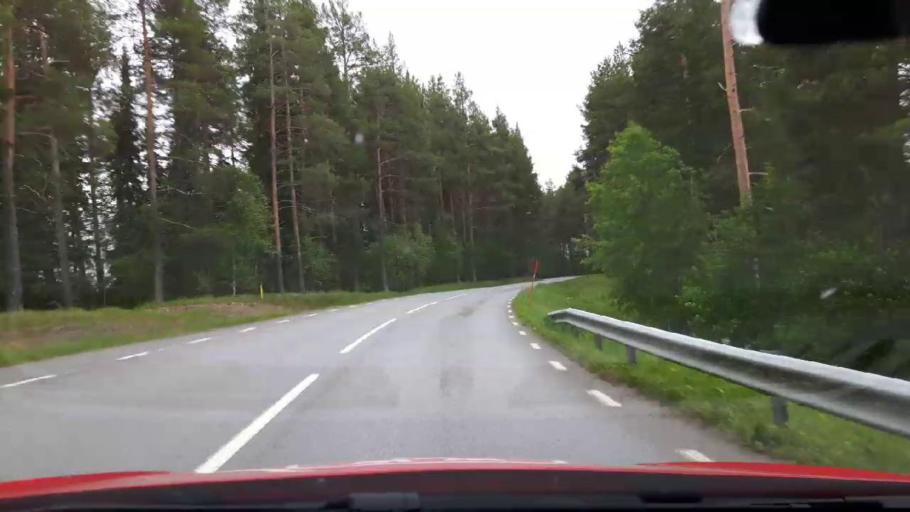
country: SE
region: Jaemtland
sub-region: Stroemsunds Kommun
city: Stroemsund
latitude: 63.5068
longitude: 15.4619
